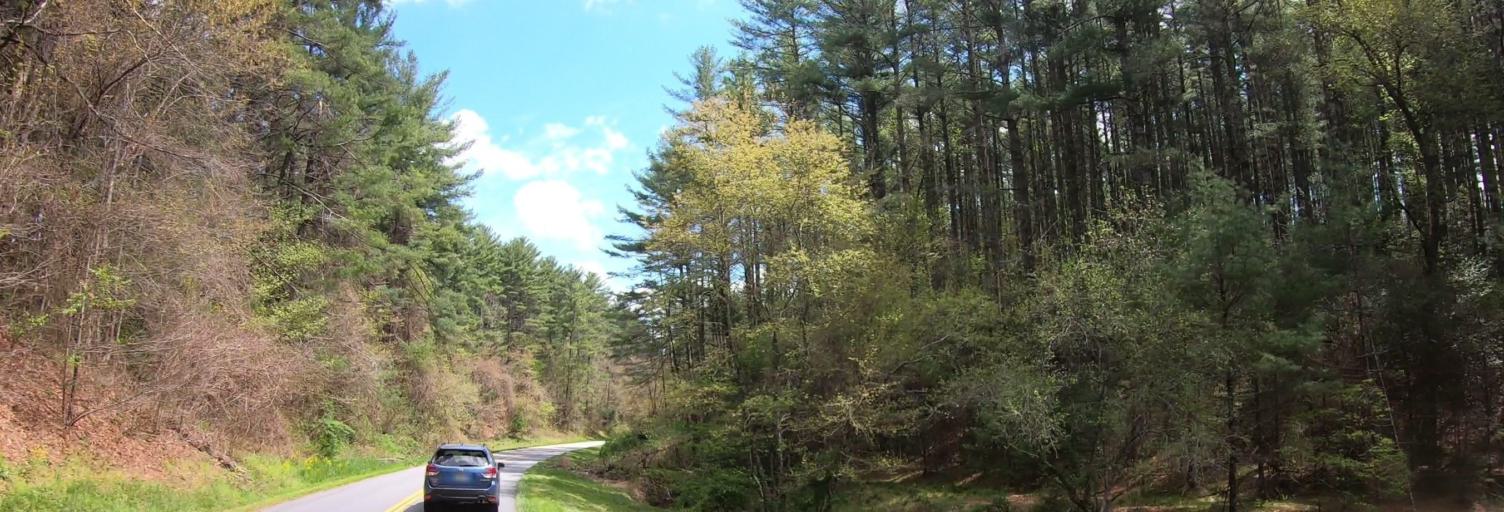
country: US
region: North Carolina
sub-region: Surry County
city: Thurmond
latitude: 36.4743
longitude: -80.9837
